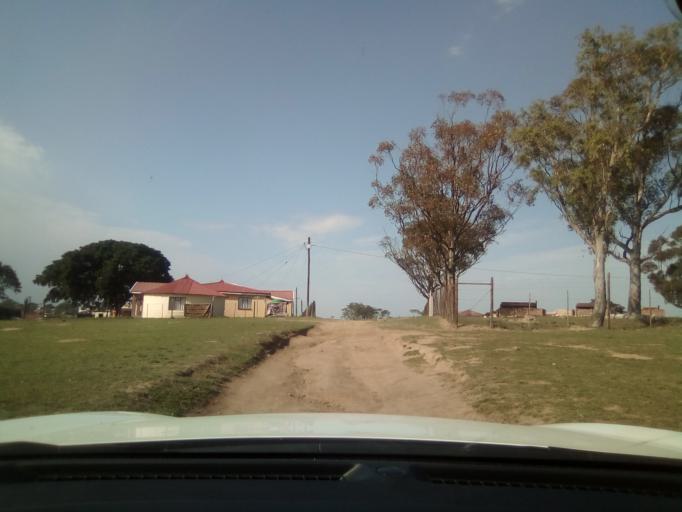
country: ZA
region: Eastern Cape
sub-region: Buffalo City Metropolitan Municipality
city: Bhisho
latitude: -32.9842
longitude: 27.2593
